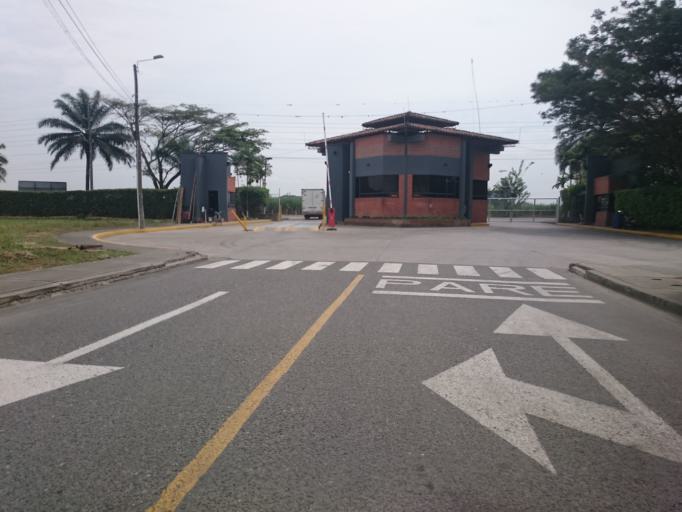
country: CO
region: Cauca
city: Puerto Tejada
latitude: 3.2113
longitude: -76.4252
